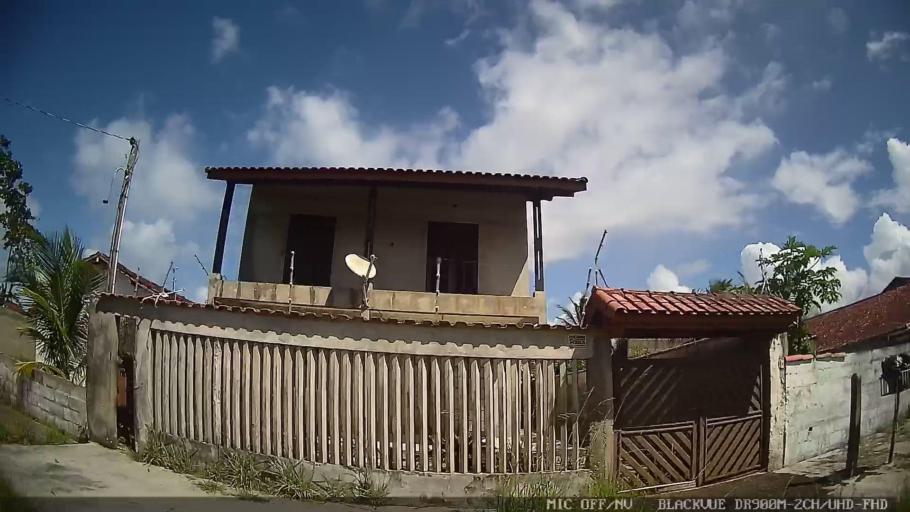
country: BR
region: Sao Paulo
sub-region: Itanhaem
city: Itanhaem
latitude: -24.2275
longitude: -46.8719
